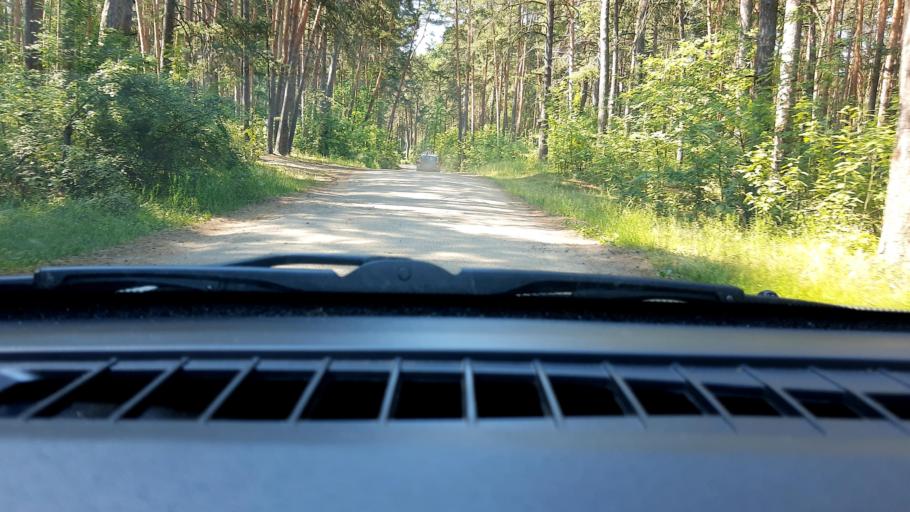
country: RU
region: Nizjnij Novgorod
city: Burevestnik
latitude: 56.1970
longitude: 43.7937
